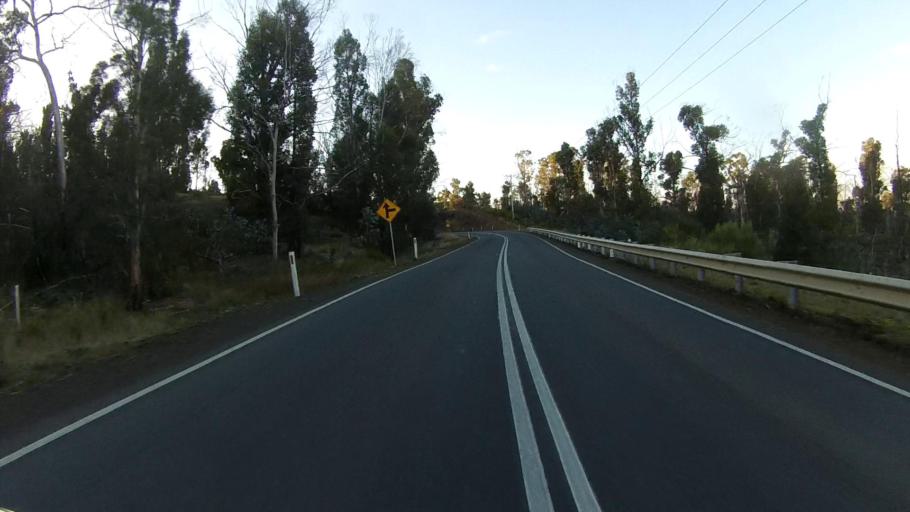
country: AU
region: Tasmania
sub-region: Sorell
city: Sorell
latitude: -42.8544
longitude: 147.8222
